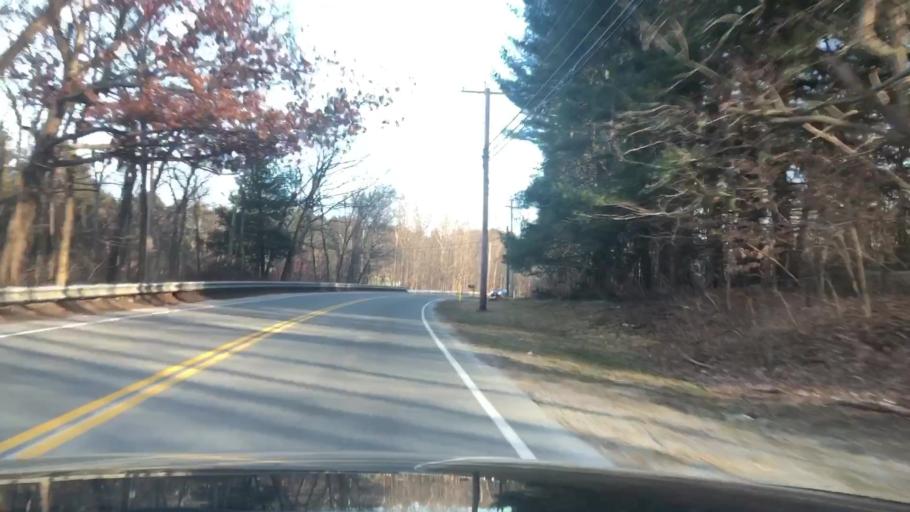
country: US
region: Massachusetts
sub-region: Worcester County
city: Bolton
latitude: 42.4458
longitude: -71.6271
